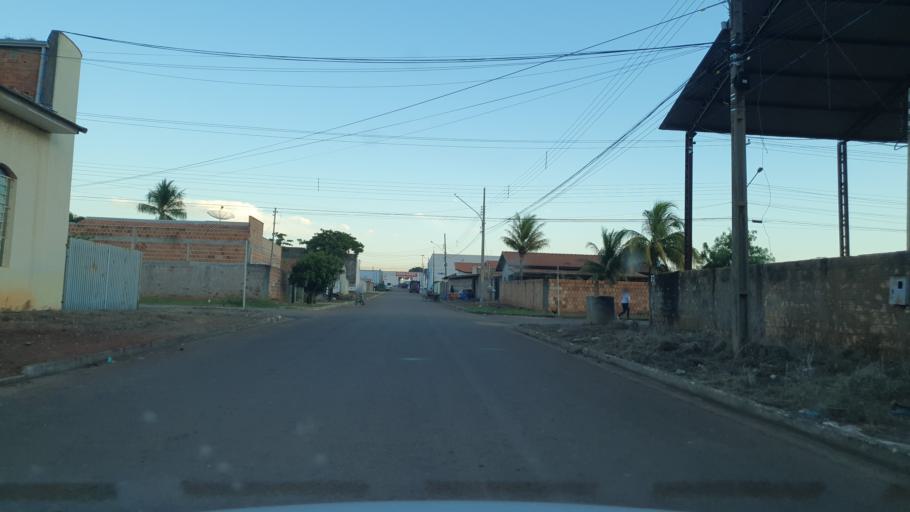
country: BR
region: Mato Grosso
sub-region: Pontes E Lacerda
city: Pontes e Lacerda
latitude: -15.2239
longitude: -59.3228
